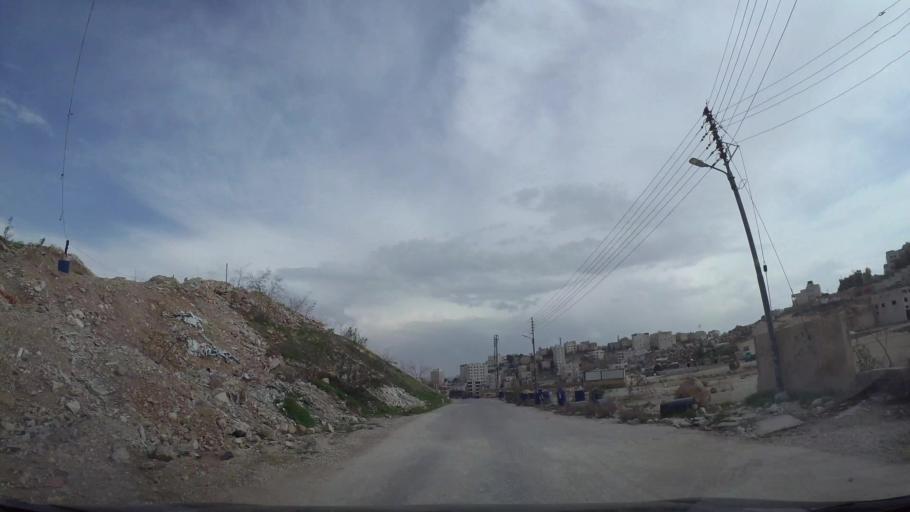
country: JO
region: Amman
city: Amman
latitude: 32.0151
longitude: 35.9459
